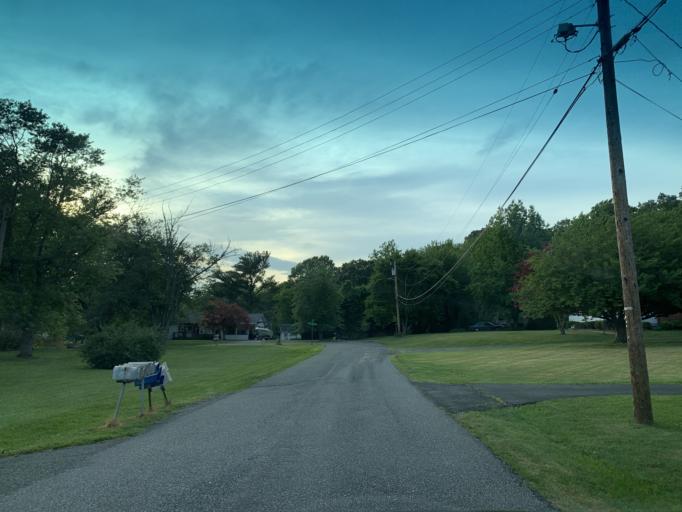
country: US
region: Maryland
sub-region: Harford County
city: Edgewood
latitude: 39.4504
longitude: -76.3008
